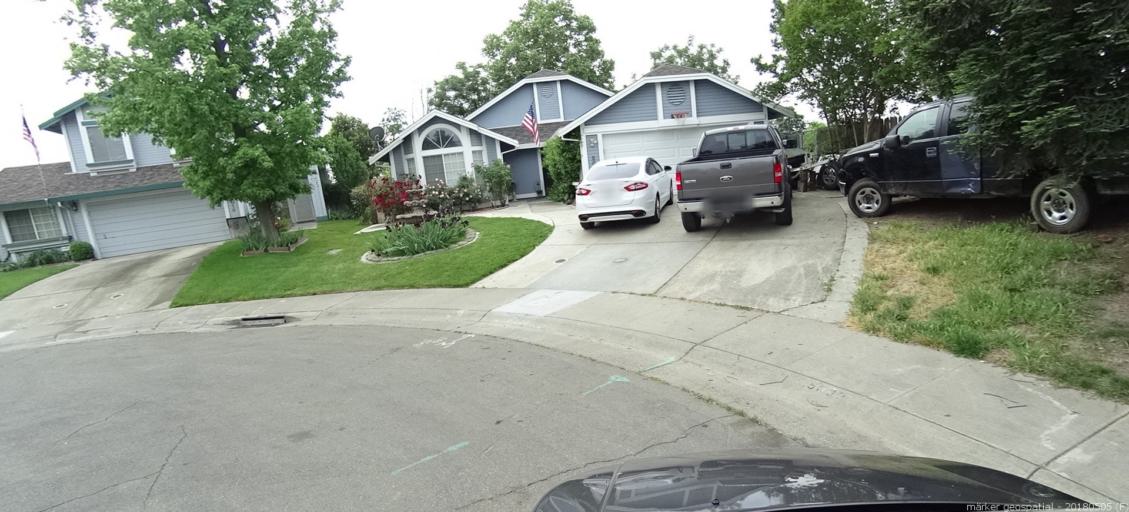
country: US
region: California
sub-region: Sacramento County
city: Rio Linda
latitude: 38.6588
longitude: -121.4400
